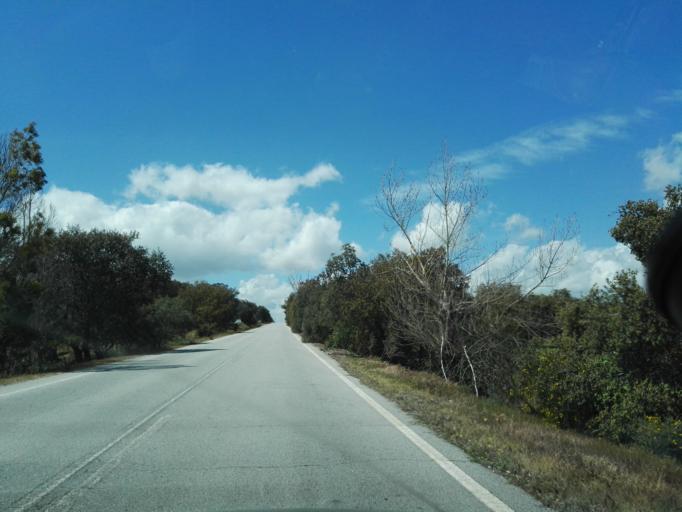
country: PT
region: Portalegre
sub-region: Campo Maior
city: Campo Maior
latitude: 38.9934
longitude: -7.1578
